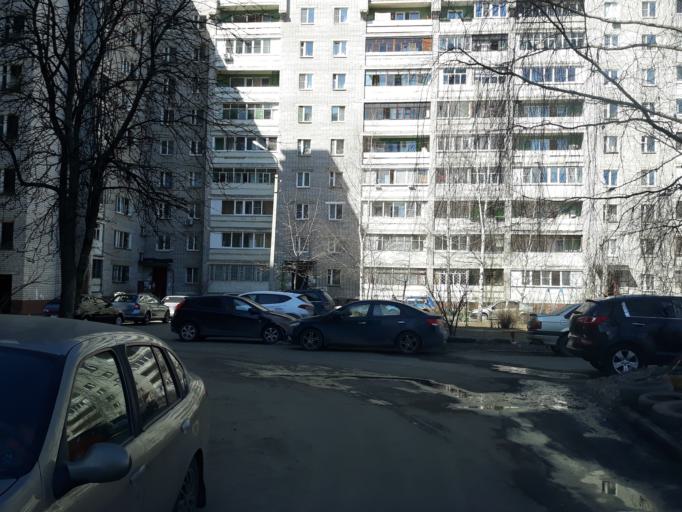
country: RU
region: Jaroslavl
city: Yaroslavl
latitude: 57.6563
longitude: 39.9487
